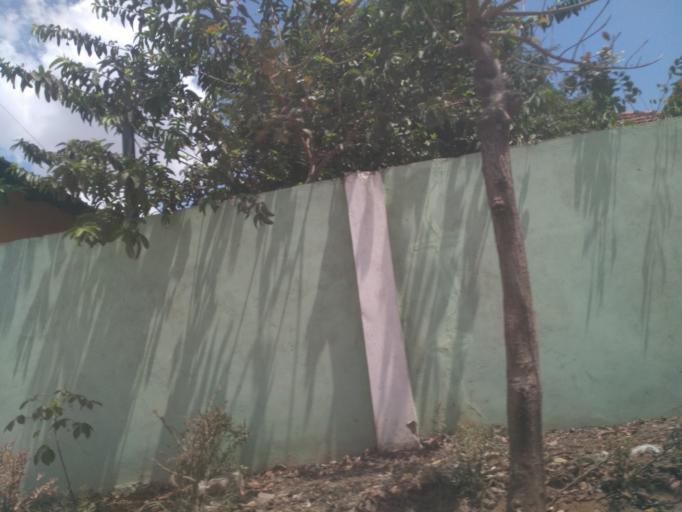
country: TZ
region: Dar es Salaam
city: Dar es Salaam
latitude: -6.8446
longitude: 39.2644
